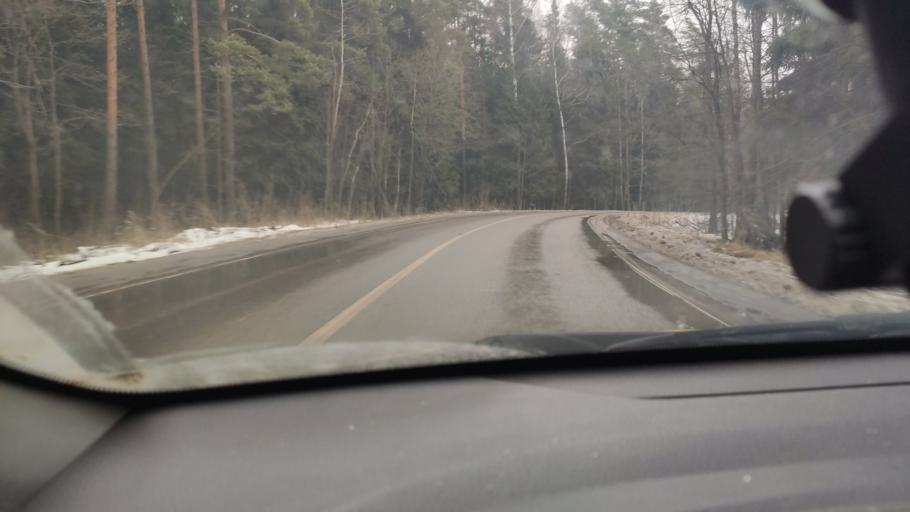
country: RU
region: Moskovskaya
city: Vostryakovo
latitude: 55.4567
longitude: 37.8665
